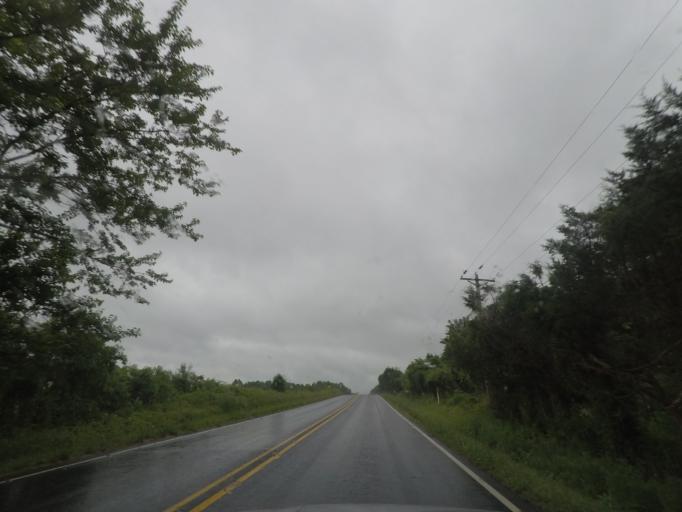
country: US
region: Virginia
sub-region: Culpeper County
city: Merrimac
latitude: 38.3696
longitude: -78.1018
